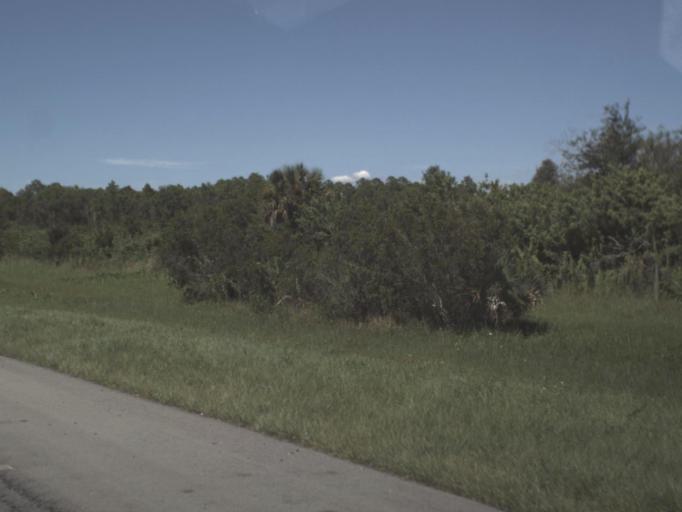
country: US
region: Florida
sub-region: Lee County
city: Suncoast Estates
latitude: 26.7525
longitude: -81.8649
